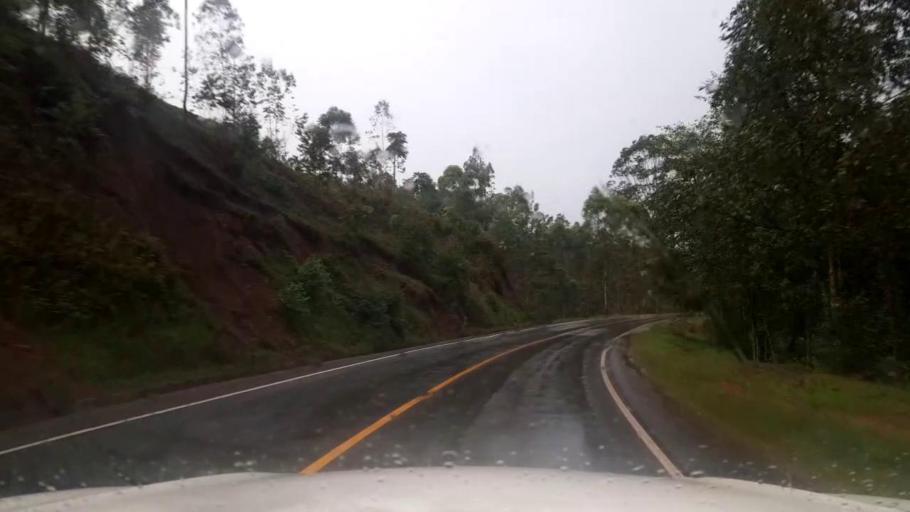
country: RW
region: Northern Province
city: Musanze
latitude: -1.5844
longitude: 29.7351
